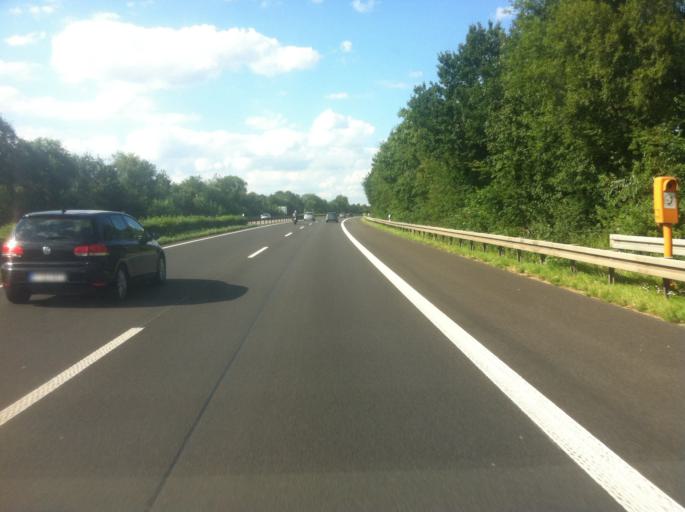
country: DE
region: North Rhine-Westphalia
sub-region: Regierungsbezirk Koln
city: Erftstadt
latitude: 50.8201
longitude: 6.7853
